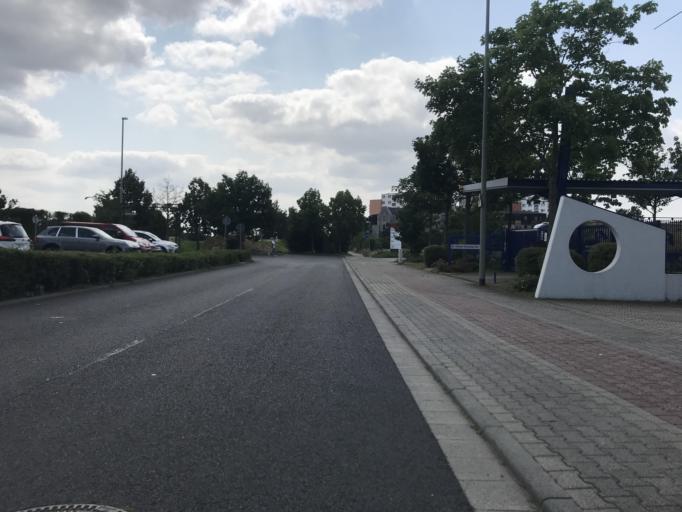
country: DE
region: Hesse
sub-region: Regierungsbezirk Darmstadt
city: Hochheim am Main
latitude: 50.0135
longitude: 8.3701
